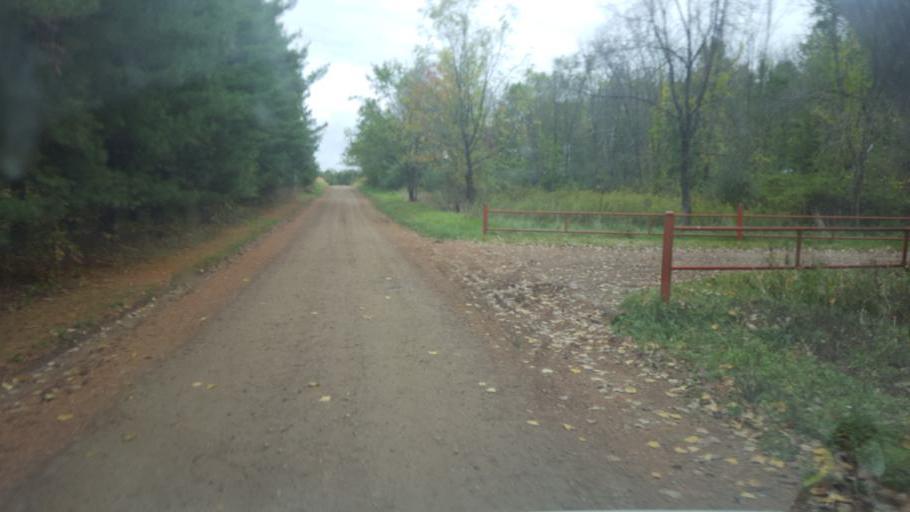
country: US
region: Ohio
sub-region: Wayne County
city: Shreve
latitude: 40.5466
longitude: -82.0887
